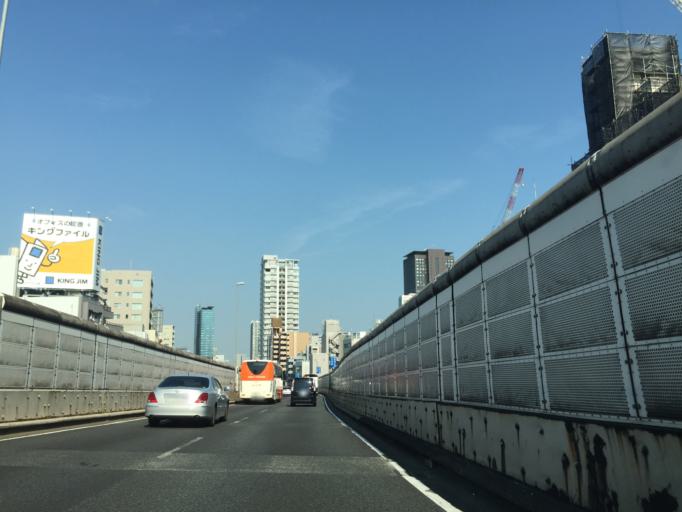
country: JP
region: Tokyo
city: Tokyo
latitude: 35.6554
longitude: 139.7406
